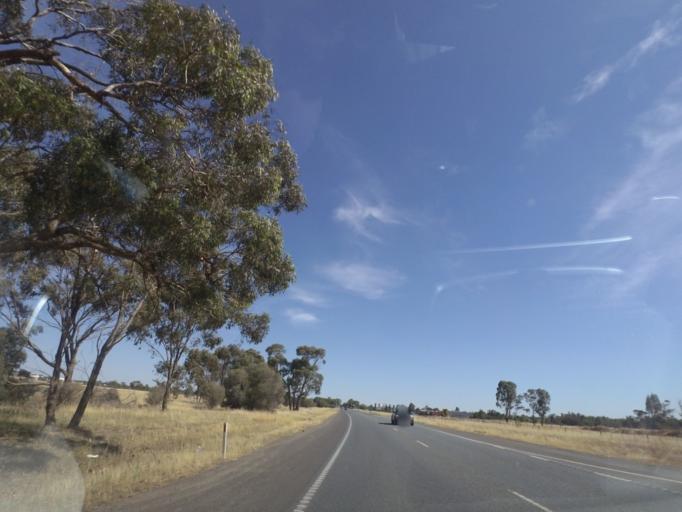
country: AU
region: Victoria
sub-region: Greater Shepparton
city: Shepparton
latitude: -36.4313
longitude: 145.3889
